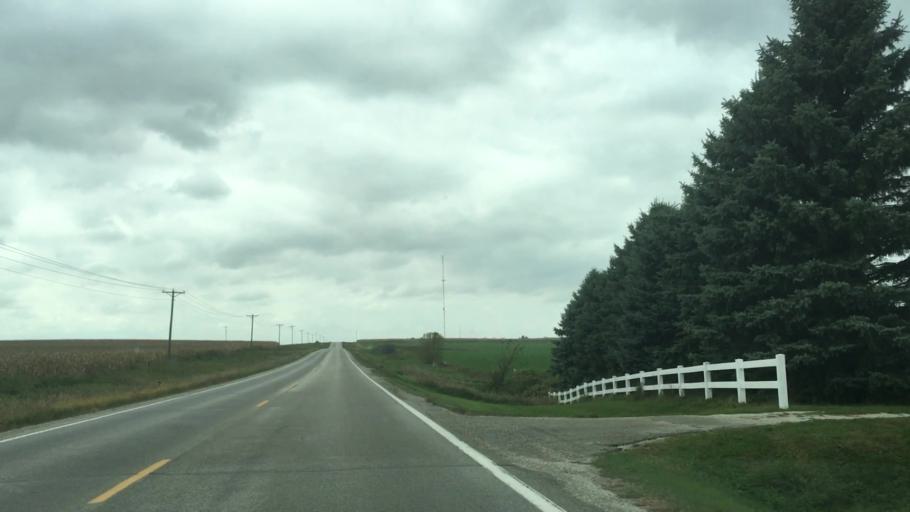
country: US
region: Minnesota
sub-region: Fillmore County
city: Preston
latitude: 43.7318
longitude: -92.0700
